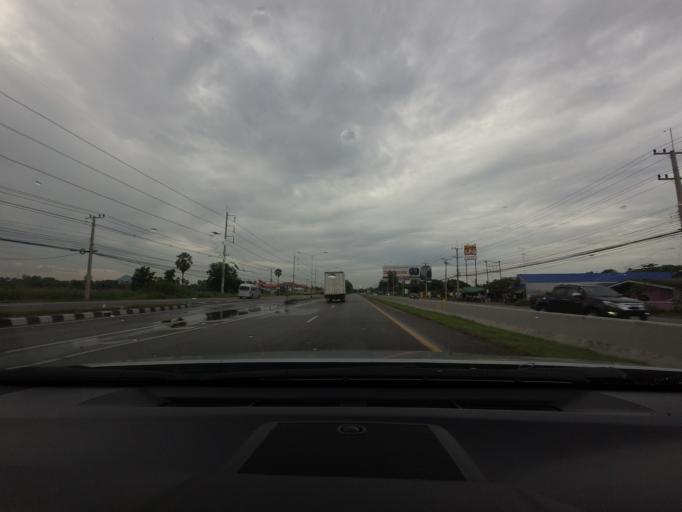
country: TH
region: Phetchaburi
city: Khao Yoi
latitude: 13.2680
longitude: 99.8211
